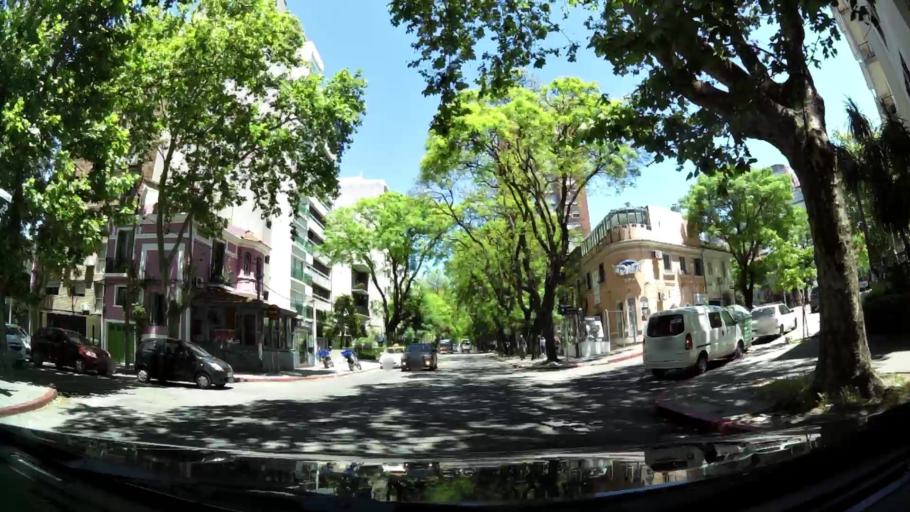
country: UY
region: Montevideo
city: Montevideo
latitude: -34.9159
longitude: -56.1542
